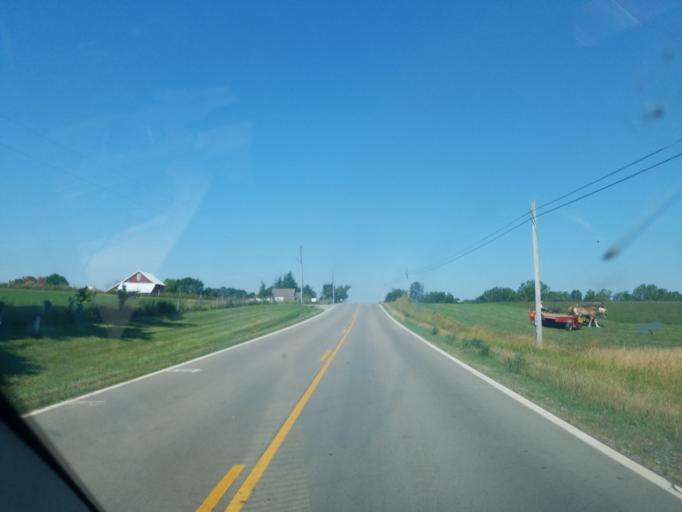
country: US
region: Ohio
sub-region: Logan County
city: Northwood
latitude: 40.4575
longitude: -83.7019
